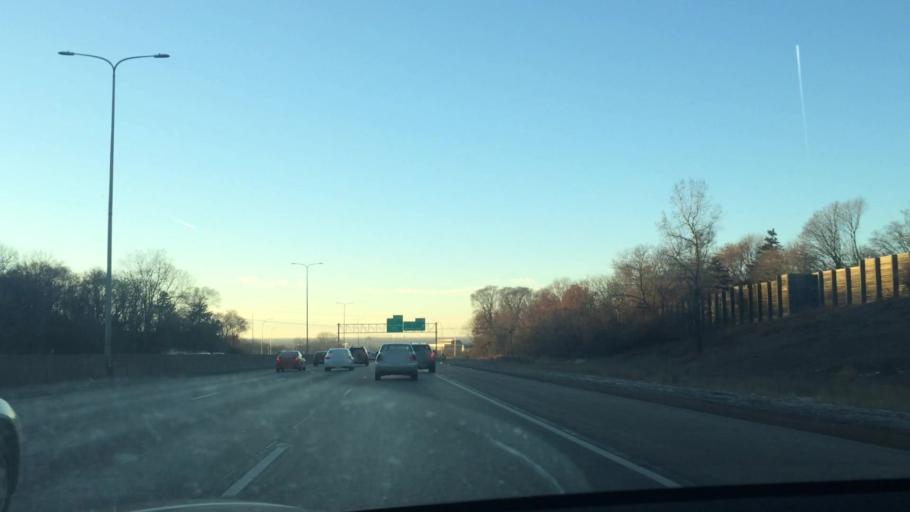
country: US
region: Minnesota
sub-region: Anoka County
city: Fridley
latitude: 45.0666
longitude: -93.2393
